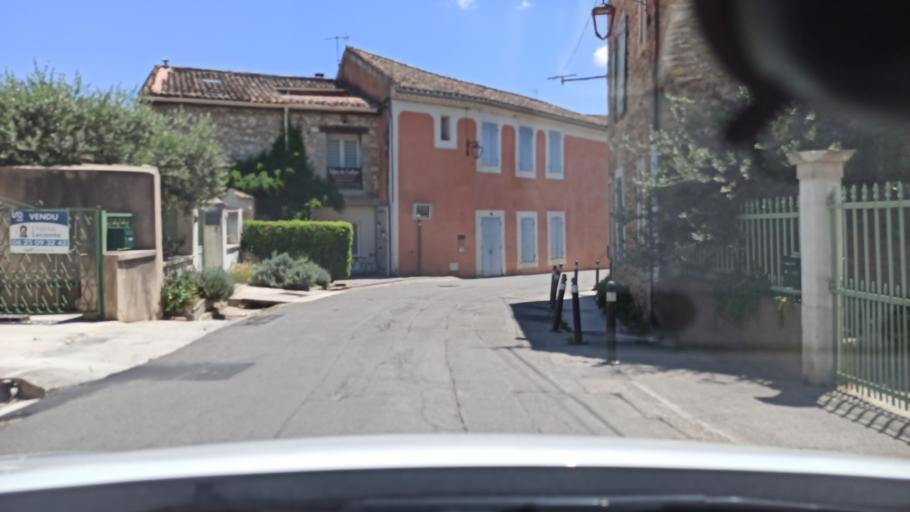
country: FR
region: Provence-Alpes-Cote d'Azur
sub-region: Departement du Vaucluse
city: Caumont-sur-Durance
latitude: 43.8937
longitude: 4.9439
